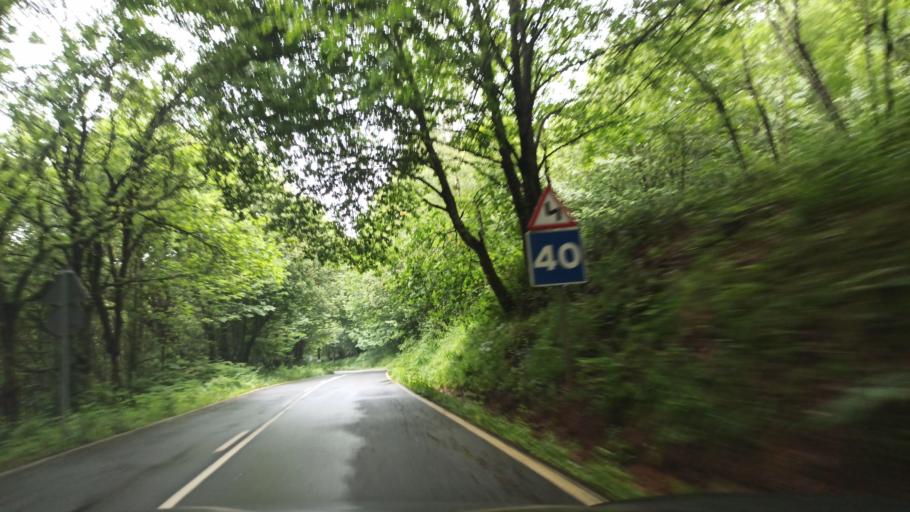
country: ES
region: Galicia
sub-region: Provincia da Coruna
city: Santiso
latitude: 42.7831
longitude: -8.0805
